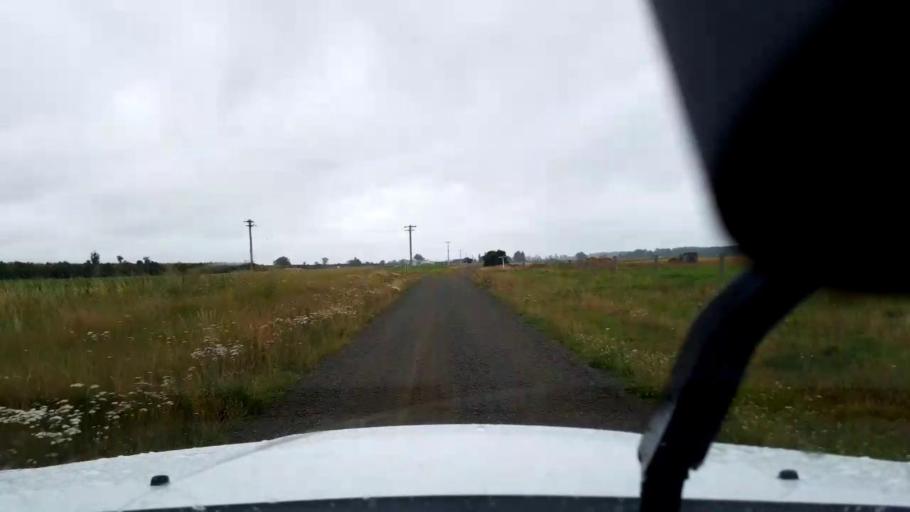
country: NZ
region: Canterbury
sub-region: Timaru District
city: Pleasant Point
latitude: -44.2535
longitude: 171.1990
